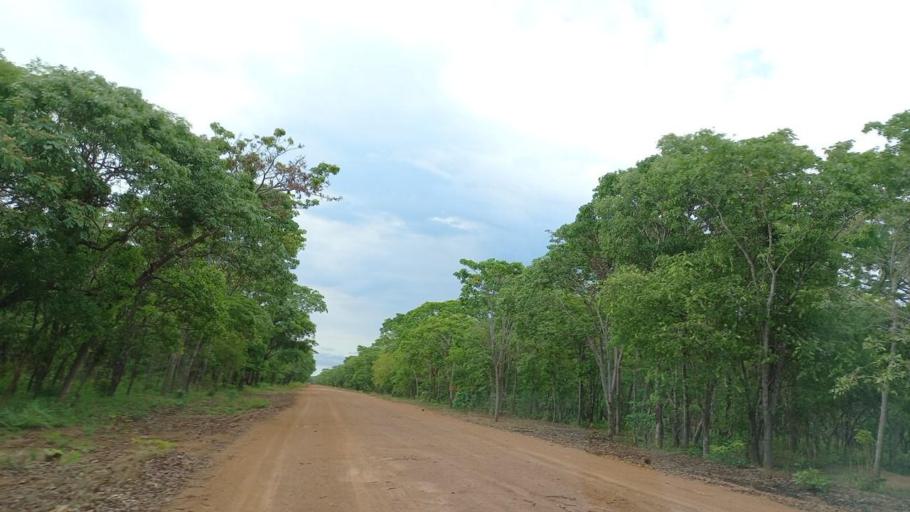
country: ZM
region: North-Western
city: Kalengwa
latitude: -13.3768
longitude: 25.0729
